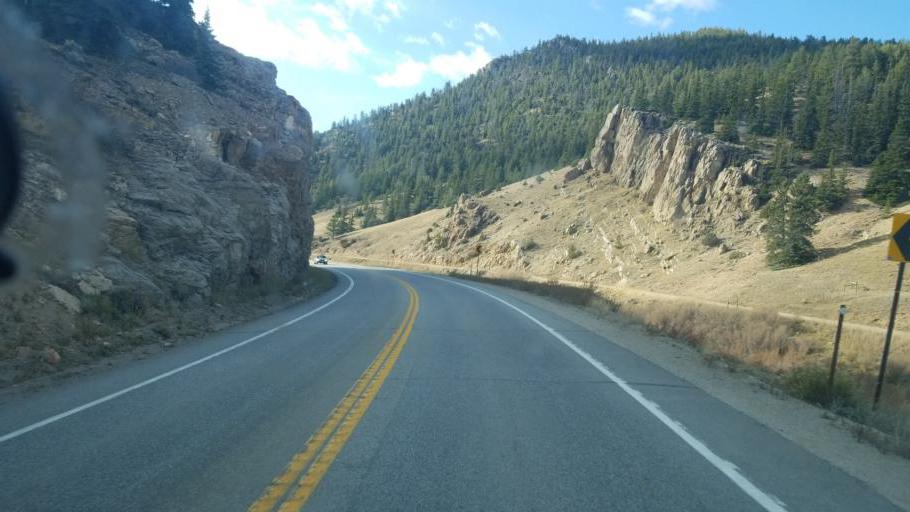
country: US
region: Colorado
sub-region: Chaffee County
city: Buena Vista
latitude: 38.8611
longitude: -105.9861
